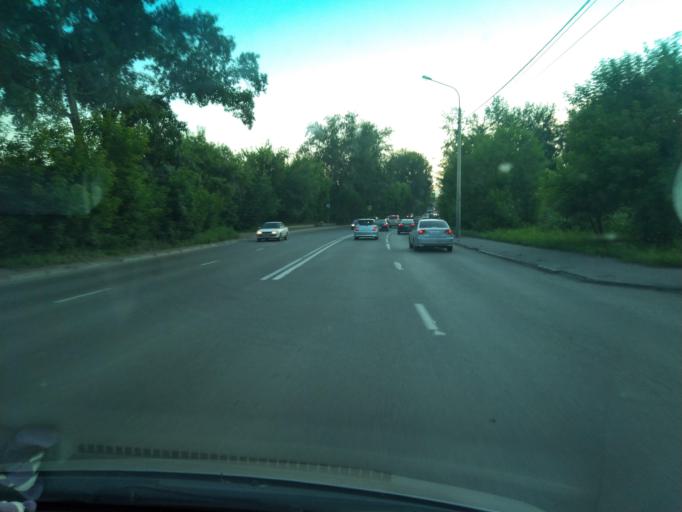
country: RU
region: Krasnoyarskiy
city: Krasnoyarsk
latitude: 55.9881
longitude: 92.9027
